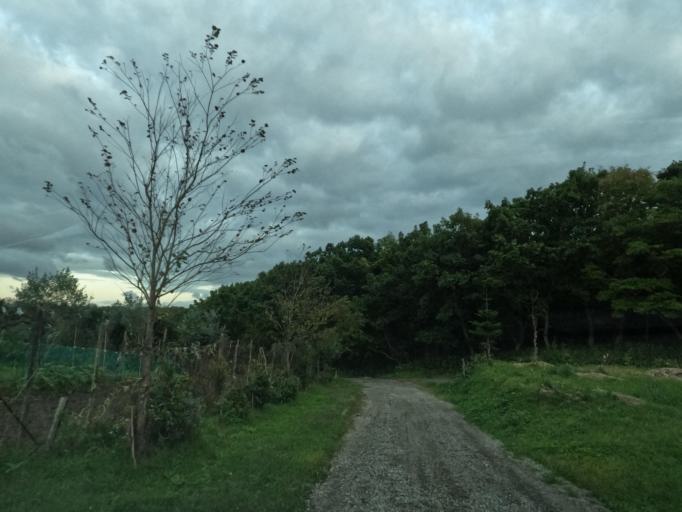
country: JP
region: Hokkaido
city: Muroran
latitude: 42.3706
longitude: 140.9715
